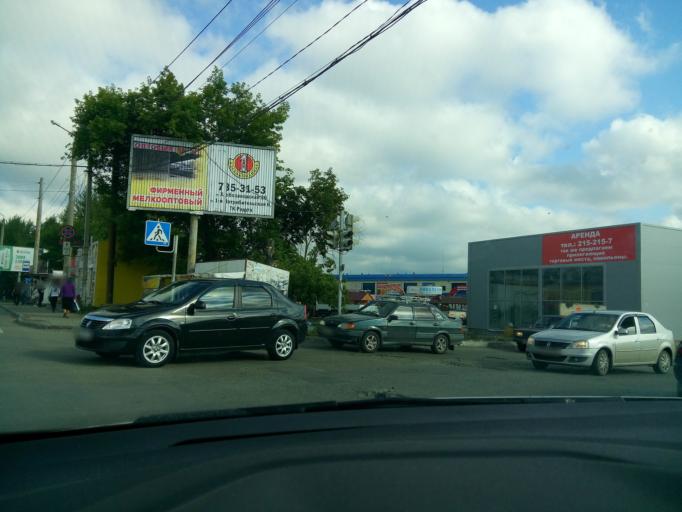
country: RU
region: Chelyabinsk
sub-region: Gorod Chelyabinsk
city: Chelyabinsk
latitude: 55.2330
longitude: 61.3687
